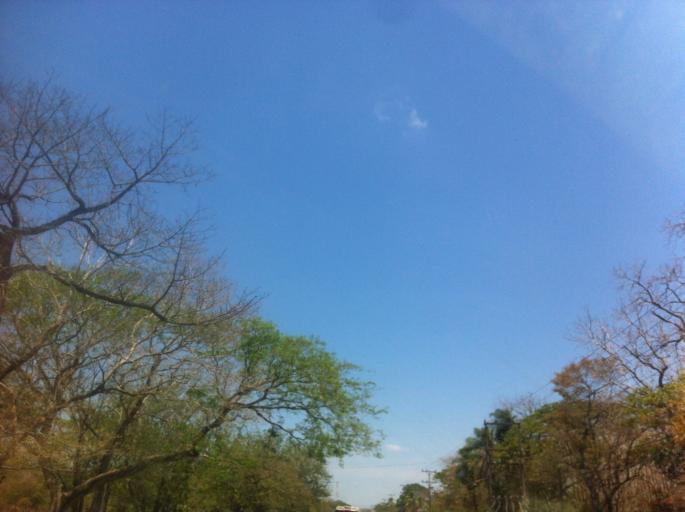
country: CR
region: Guanacaste
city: Sardinal
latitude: 10.4927
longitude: -85.5701
